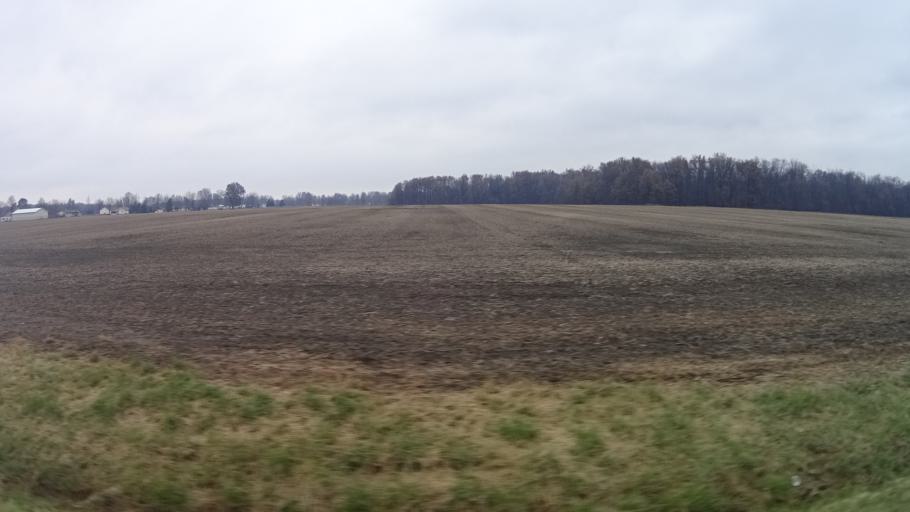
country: US
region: Ohio
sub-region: Lorain County
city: Lagrange
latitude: 41.2524
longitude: -82.0971
